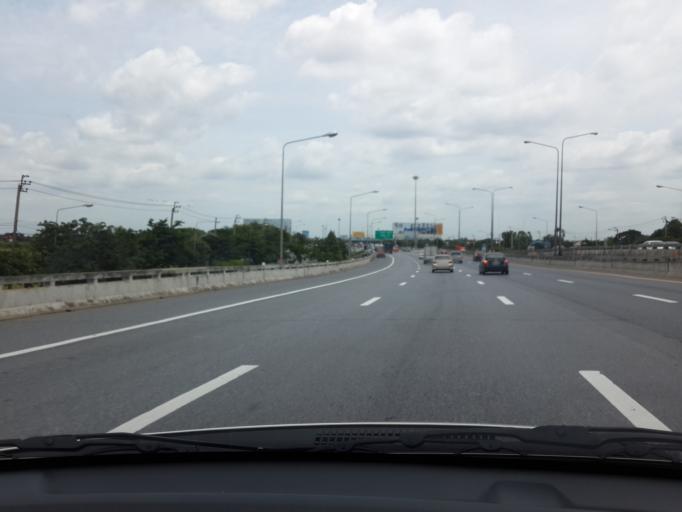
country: TH
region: Bangkok
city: Saphan Sung
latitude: 13.7494
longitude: 100.7022
